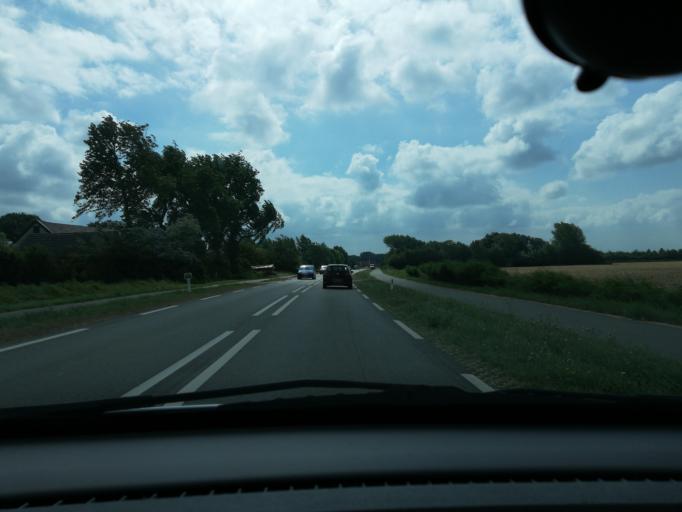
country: NL
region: Zeeland
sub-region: Gemeente Middelburg
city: Middelburg
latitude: 51.5591
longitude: 3.5820
